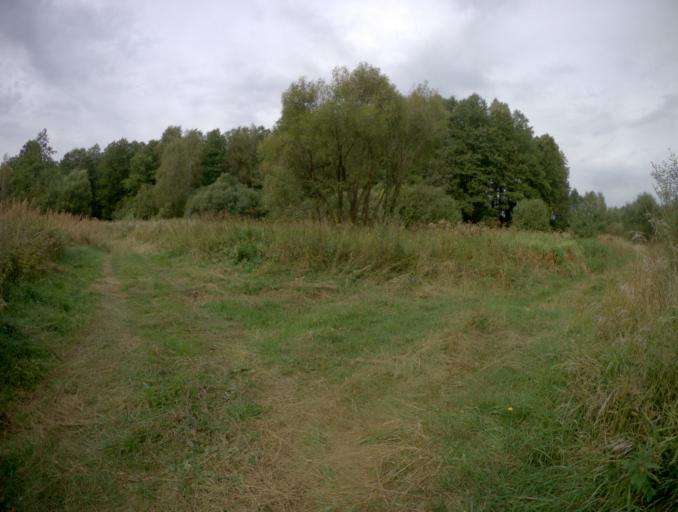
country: RU
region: Vladimir
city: Golovino
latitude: 55.9166
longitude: 40.4212
